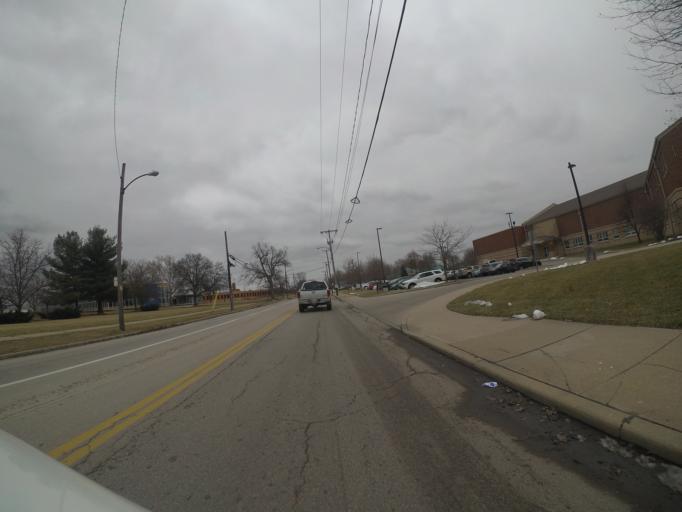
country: US
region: Ohio
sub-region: Lucas County
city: Oregon
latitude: 41.6217
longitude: -83.5151
